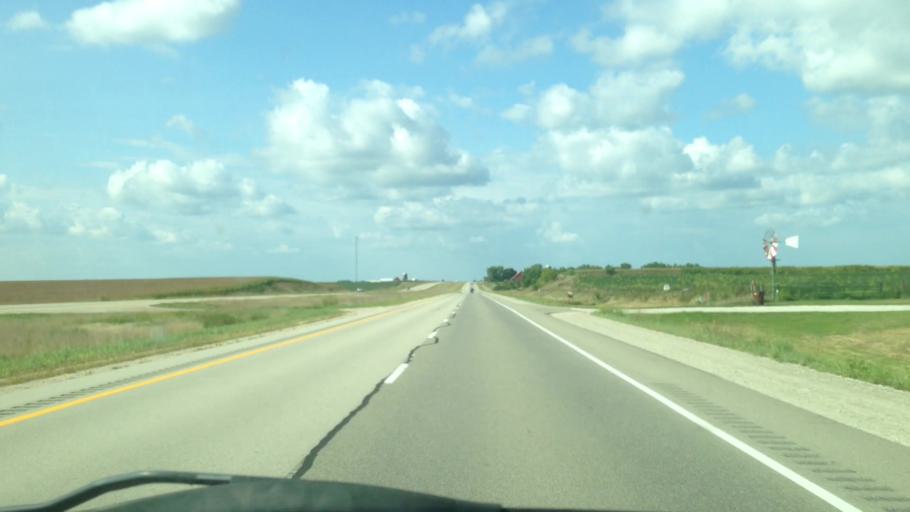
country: US
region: Iowa
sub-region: Henry County
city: Mount Pleasant
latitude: 40.8001
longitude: -91.5637
